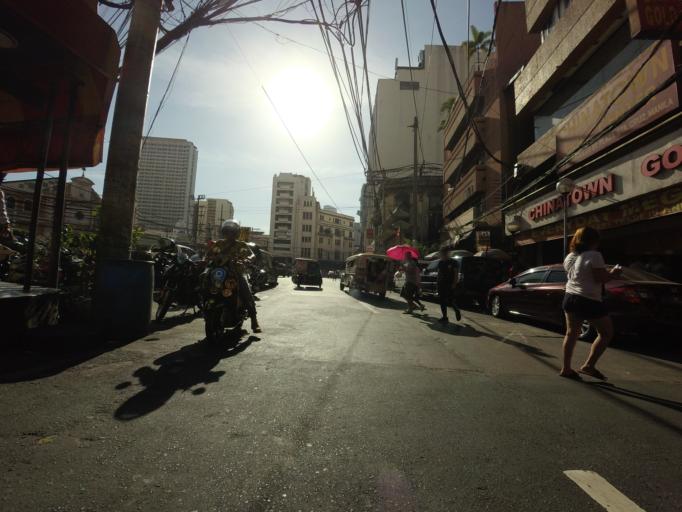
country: PH
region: Metro Manila
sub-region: City of Manila
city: Quiapo
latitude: 14.6002
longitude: 120.9806
